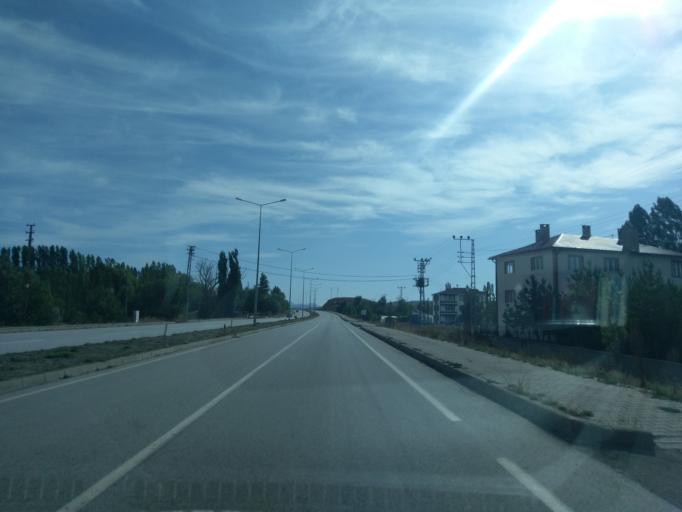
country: TR
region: Sivas
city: Imranli
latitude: 39.8707
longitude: 38.1209
